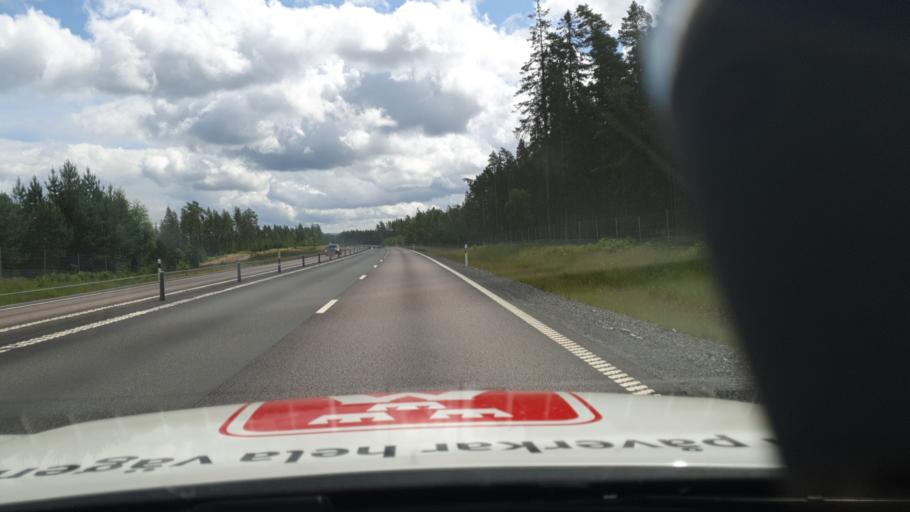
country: SE
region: Joenkoeping
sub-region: Mullsjo Kommun
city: Mullsjoe
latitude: 57.8677
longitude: 13.9614
